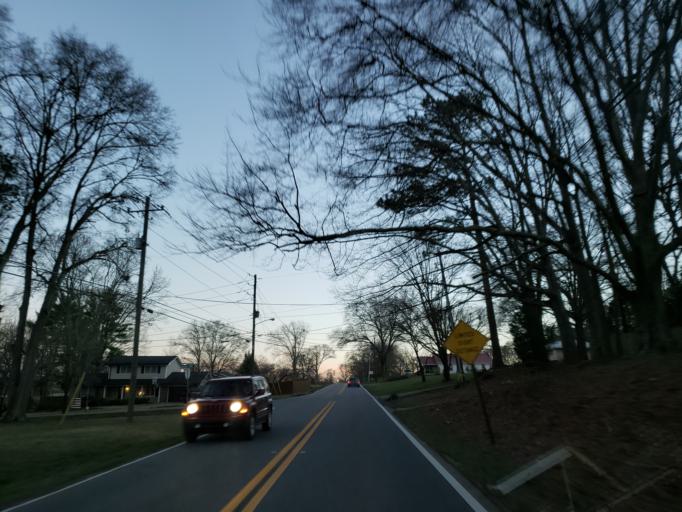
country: US
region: Georgia
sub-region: Bartow County
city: Cartersville
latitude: 34.1973
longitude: -84.8196
